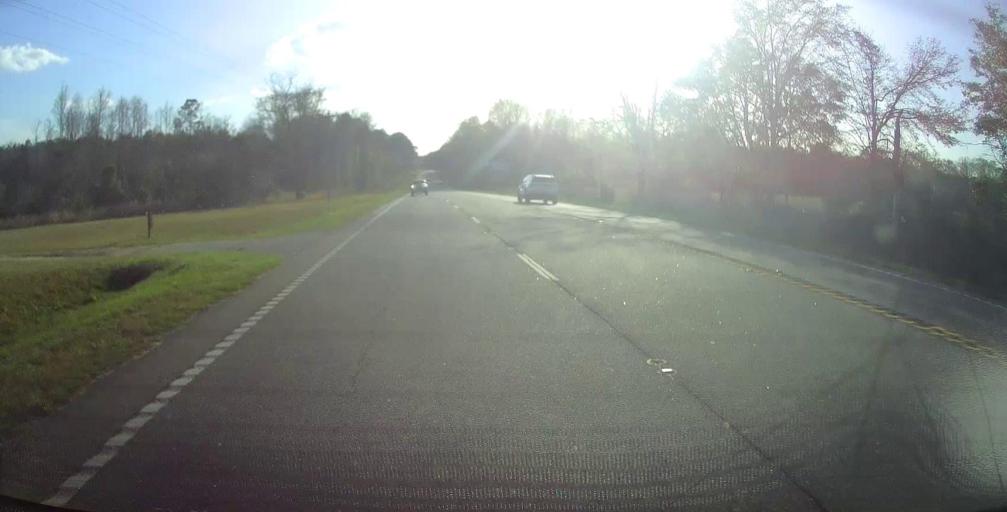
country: US
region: Georgia
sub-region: Tattnall County
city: Reidsville
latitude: 32.1024
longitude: -82.0986
